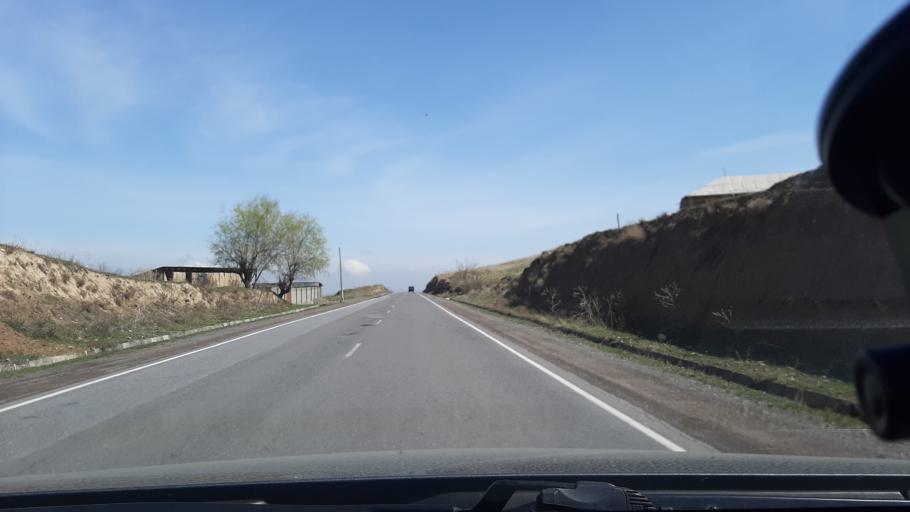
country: TJ
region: Viloyati Sughd
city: Shahriston
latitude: 39.7664
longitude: 68.8198
